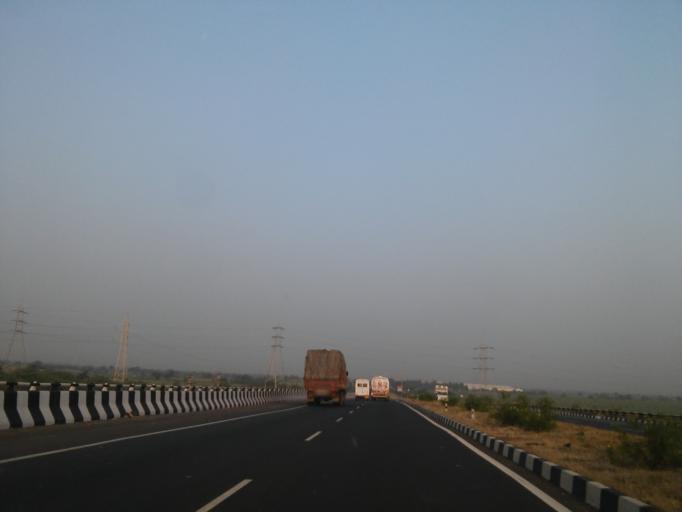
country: IN
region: Gujarat
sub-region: Kachchh
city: Bhachau
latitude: 23.2685
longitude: 70.6238
